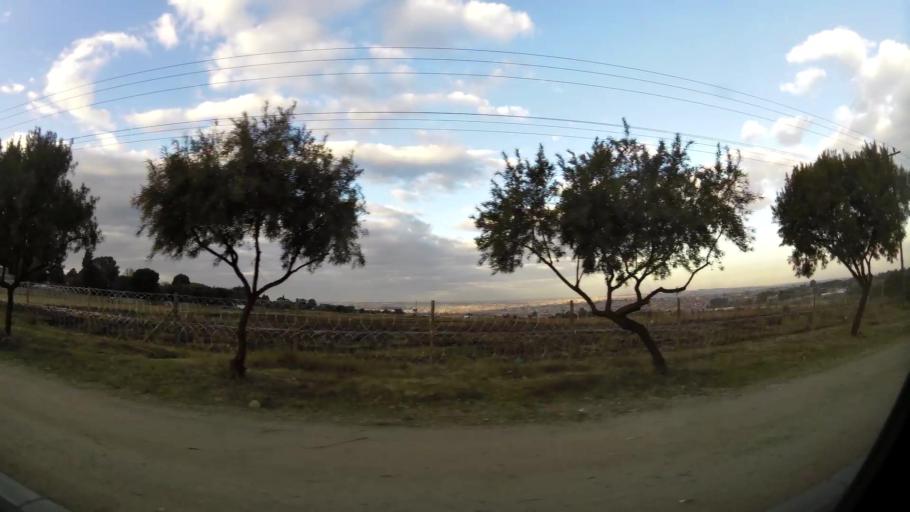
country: ZA
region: Gauteng
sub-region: City of Johannesburg Metropolitan Municipality
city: Midrand
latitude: -25.9949
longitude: 28.1549
